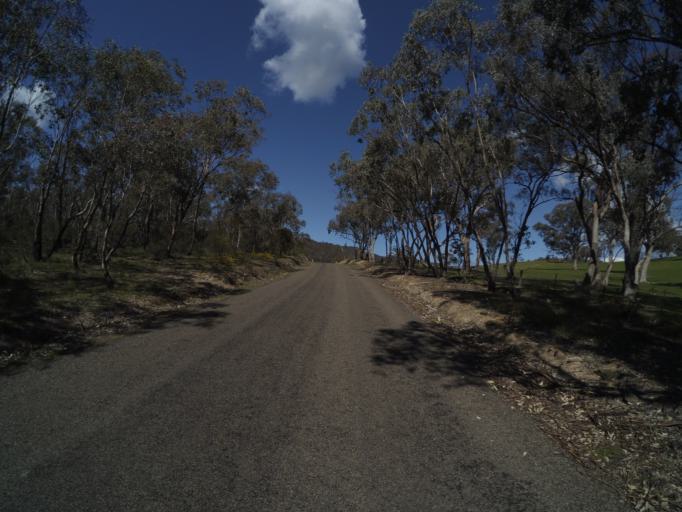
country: AU
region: New South Wales
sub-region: Yass Valley
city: Murrumbateman
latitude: -35.0714
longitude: 148.8376
